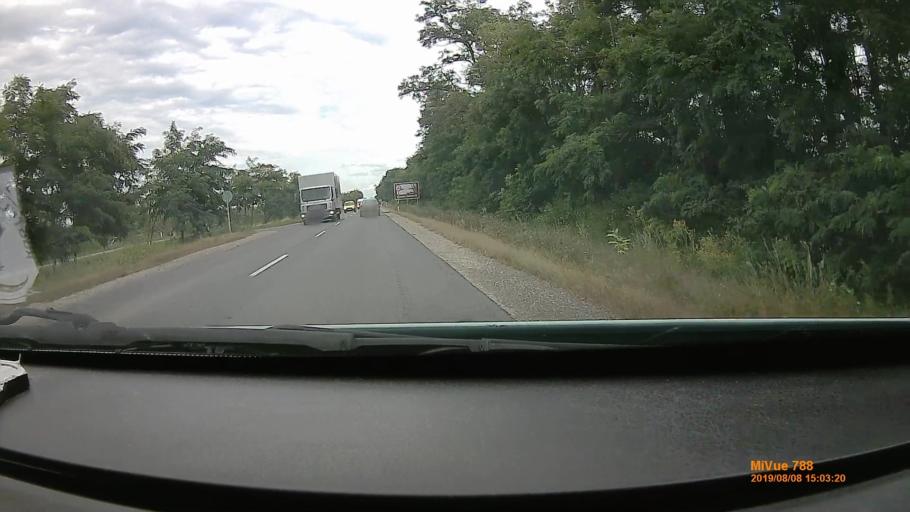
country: HU
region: Szabolcs-Szatmar-Bereg
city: Kocsord
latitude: 47.9381
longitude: 22.4098
